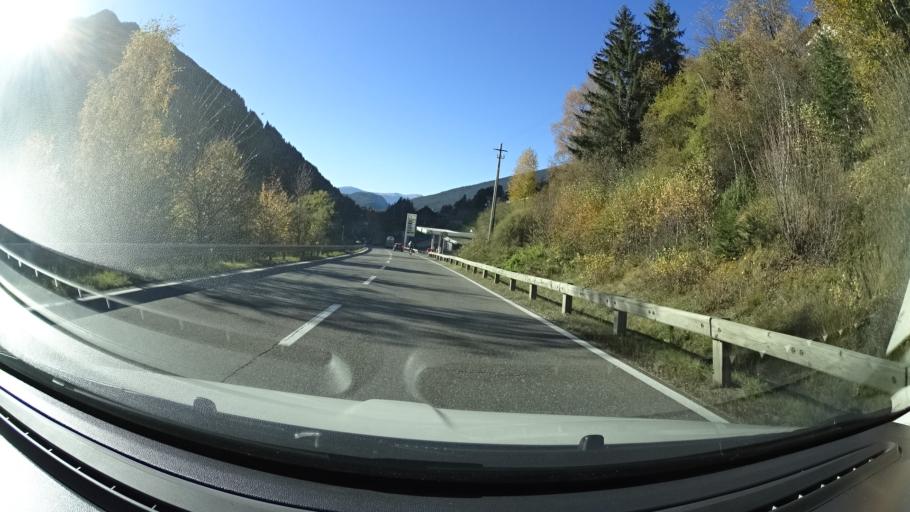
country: IT
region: Trentino-Alto Adige
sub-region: Bolzano
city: Ortisei
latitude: 46.5655
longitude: 11.6923
